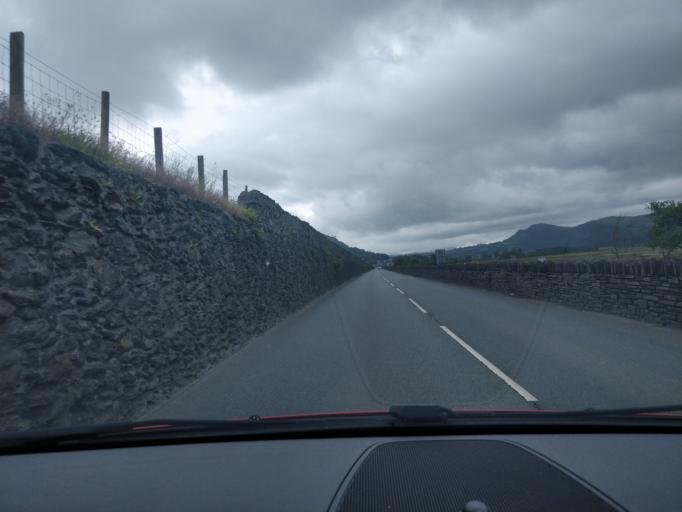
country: GB
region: Wales
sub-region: Gwynedd
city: Porthmadog
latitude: 52.9197
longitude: -4.1086
